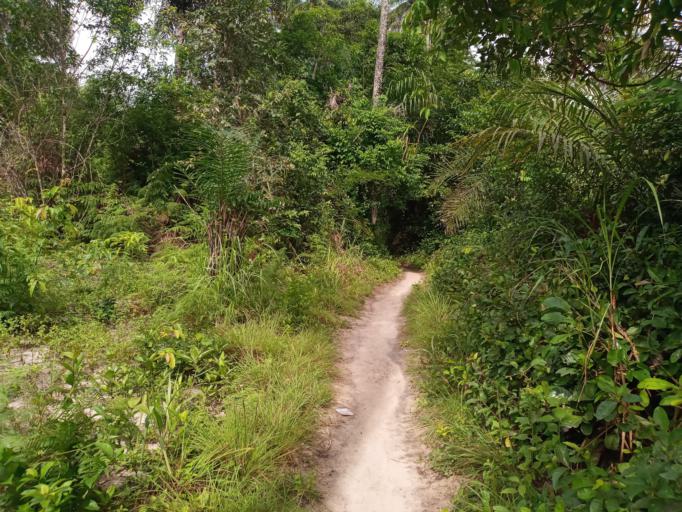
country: SL
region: Southern Province
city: Bonthe
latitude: 7.5150
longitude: -12.5464
